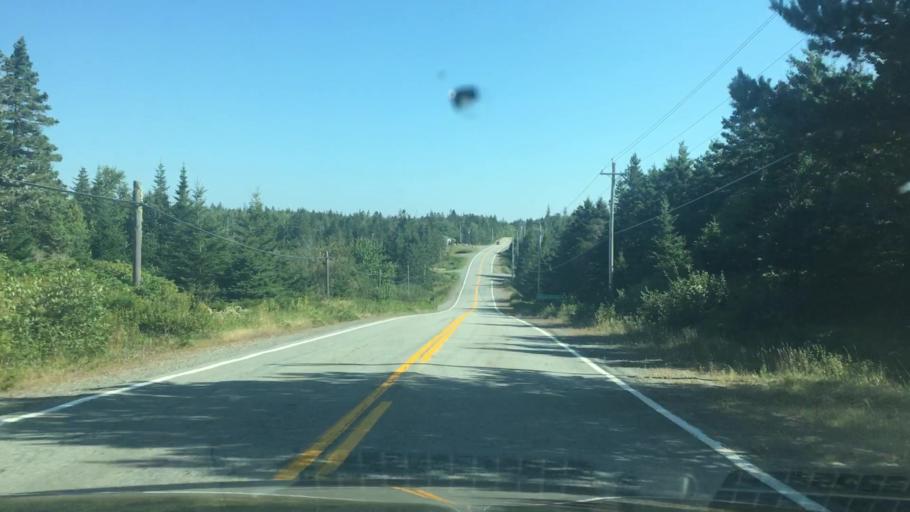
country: CA
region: Nova Scotia
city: Cole Harbour
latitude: 44.8000
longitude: -62.7151
